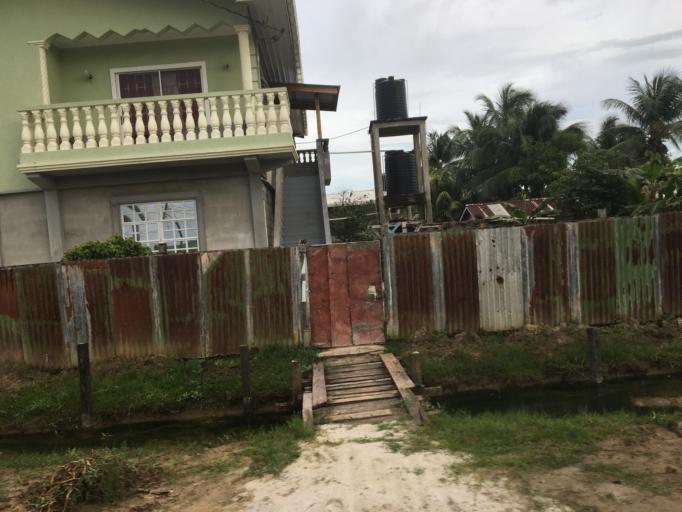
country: GY
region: Demerara-Mahaica
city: Georgetown
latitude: 6.7941
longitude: -58.1226
